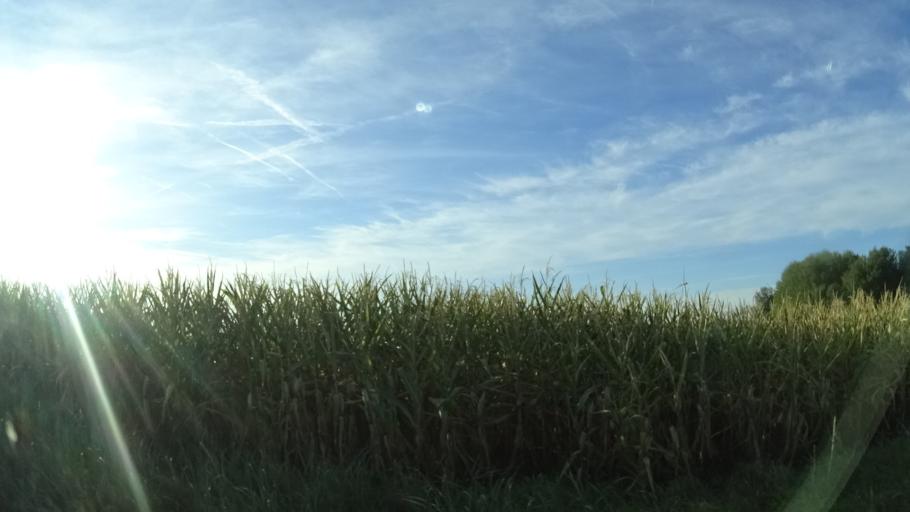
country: DE
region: Hesse
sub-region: Regierungsbezirk Darmstadt
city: Wachtersbach
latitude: 50.2938
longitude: 9.2633
